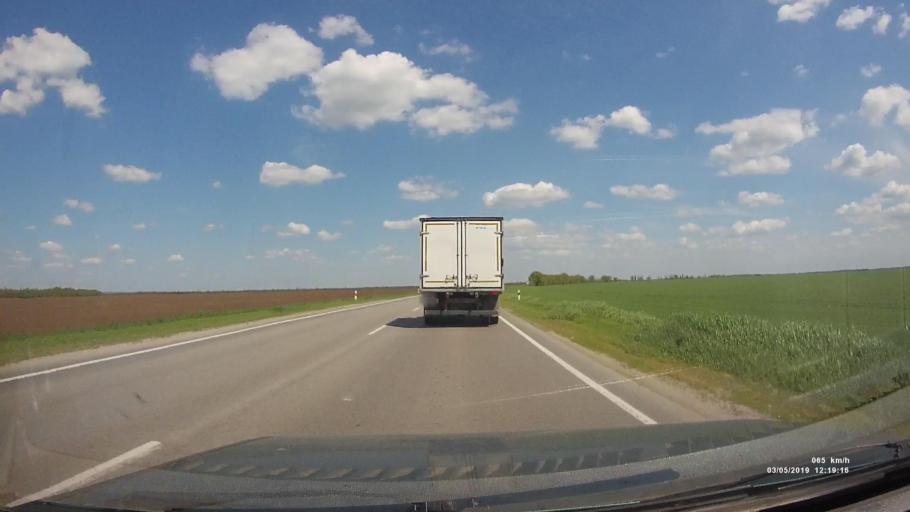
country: RU
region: Rostov
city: Melikhovskaya
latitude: 47.3993
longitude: 40.6060
